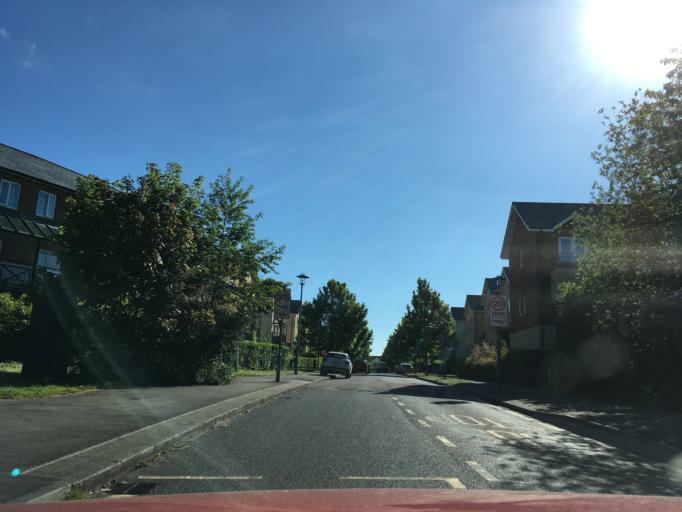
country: GB
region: England
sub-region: North Somerset
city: Portishead
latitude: 51.4845
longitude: -2.7562
